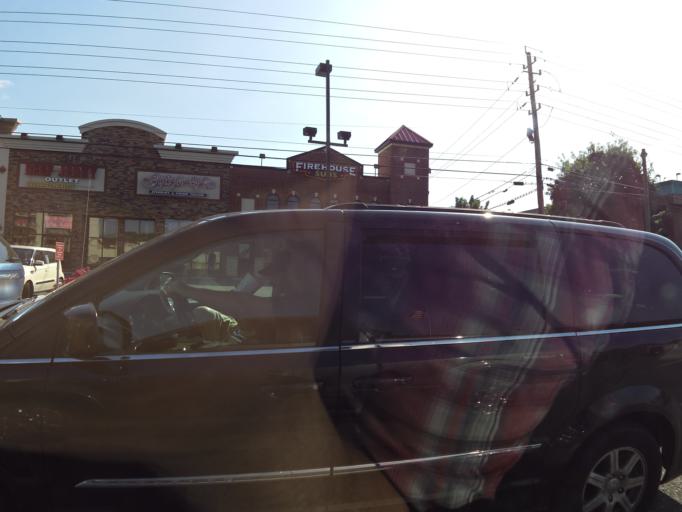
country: US
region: Tennessee
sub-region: Sevier County
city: Pigeon Forge
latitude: 35.8019
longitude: -83.5735
